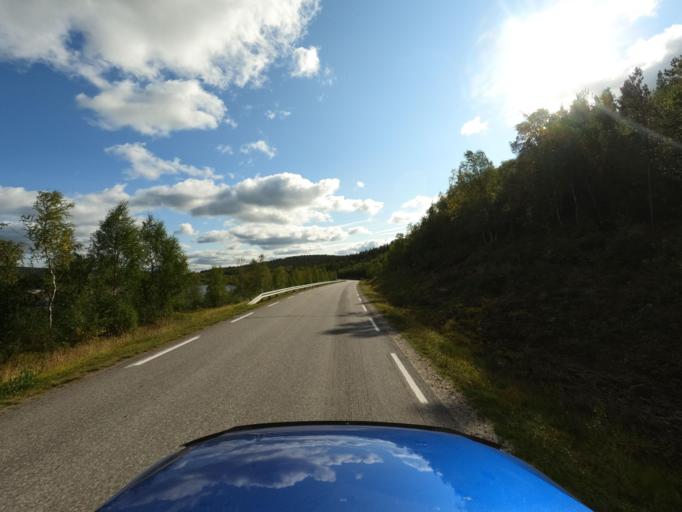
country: NO
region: Finnmark Fylke
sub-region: Karasjok
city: Karasjohka
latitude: 69.4512
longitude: 25.5822
